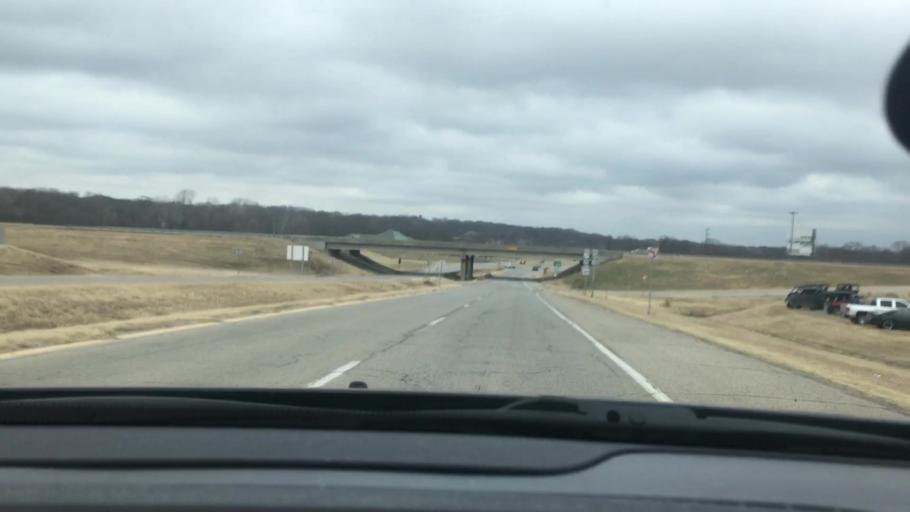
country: US
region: Oklahoma
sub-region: Bryan County
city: Durant
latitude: 34.0360
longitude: -96.3739
